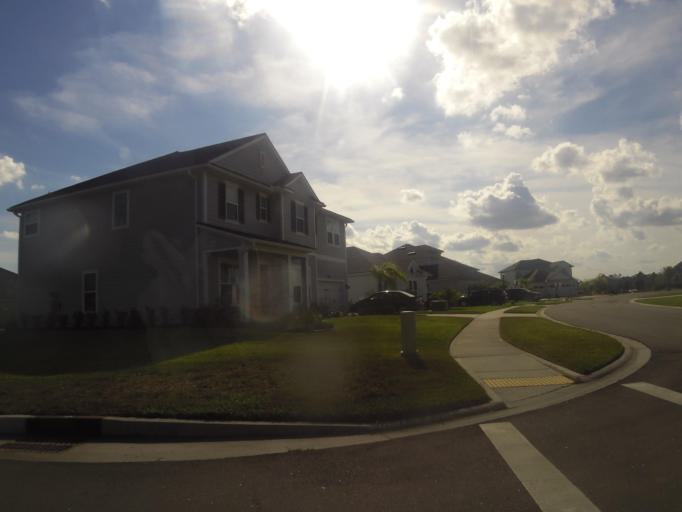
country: US
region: Florida
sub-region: Saint Johns County
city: Saint Augustine
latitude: 29.9252
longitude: -81.4907
